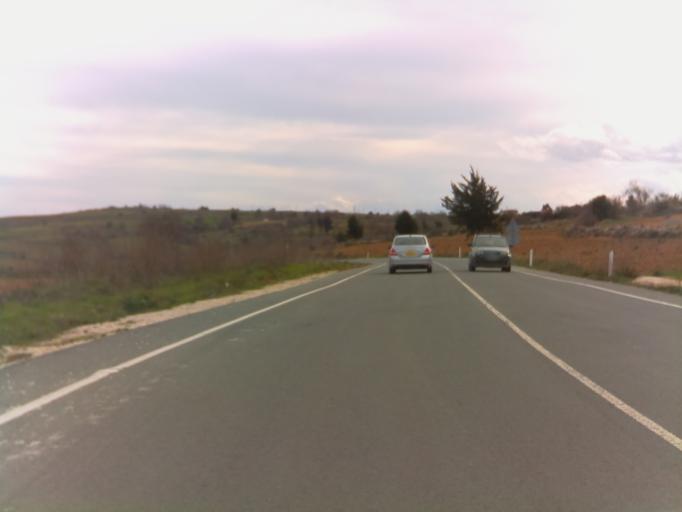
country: CY
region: Pafos
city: Pegeia
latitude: 34.9479
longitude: 32.4118
